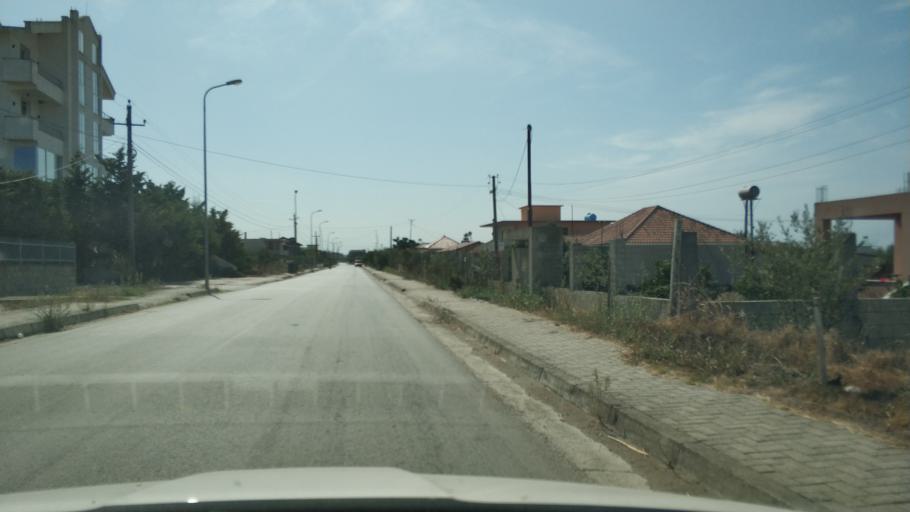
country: AL
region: Fier
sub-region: Rrethi i Lushnjes
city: Divjake
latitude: 40.9742
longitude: 19.5357
